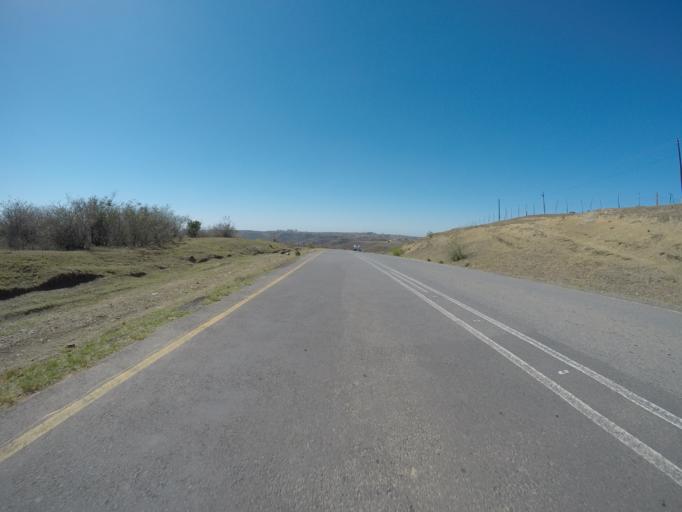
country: ZA
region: Eastern Cape
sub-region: OR Tambo District Municipality
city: Mthatha
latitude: -31.8983
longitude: 28.9448
